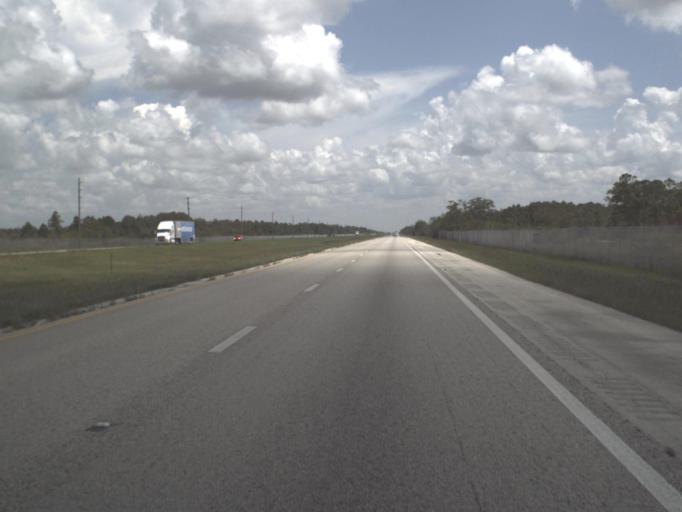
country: US
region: Florida
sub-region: Collier County
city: Immokalee
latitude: 26.1691
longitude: -81.0354
